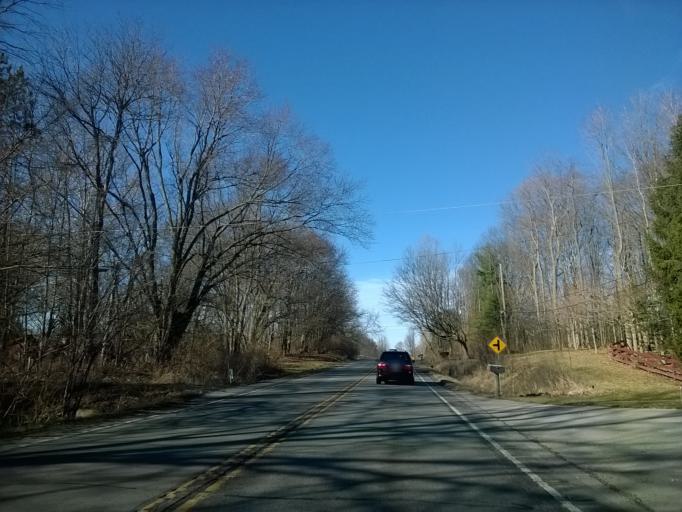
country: US
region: Indiana
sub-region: Boone County
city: Zionsville
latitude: 39.9659
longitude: -86.2489
